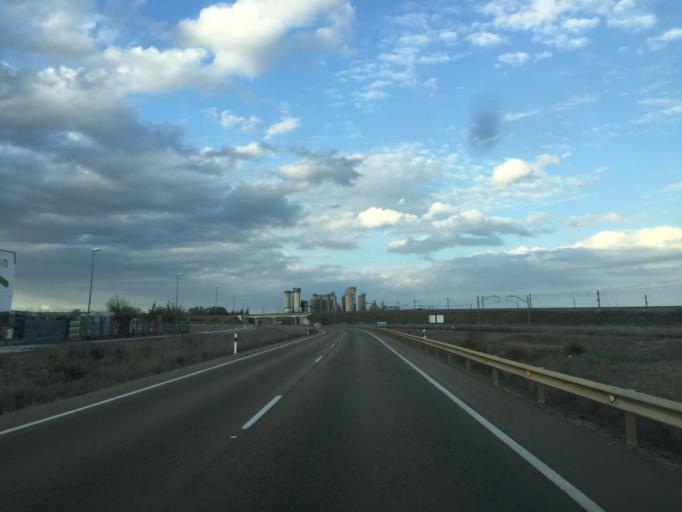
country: ES
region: Castille and Leon
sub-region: Provincia de Palencia
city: Venta de Banos
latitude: 41.9350
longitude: -4.4766
